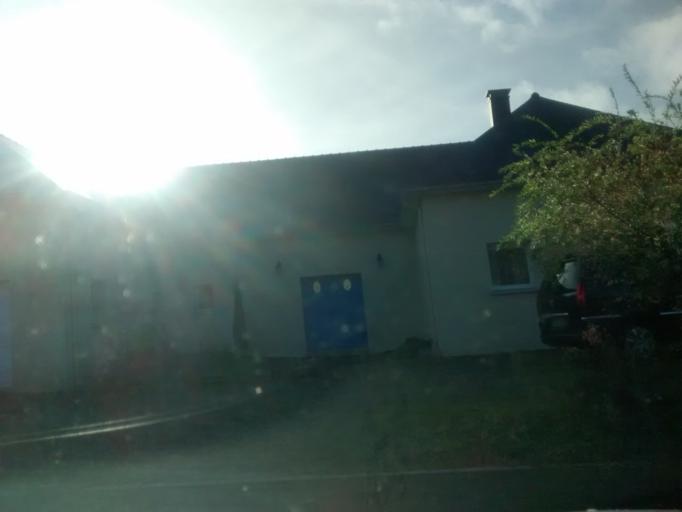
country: FR
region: Brittany
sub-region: Departement d'Ille-et-Vilaine
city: Chantepie
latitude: 48.0987
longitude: -1.6040
